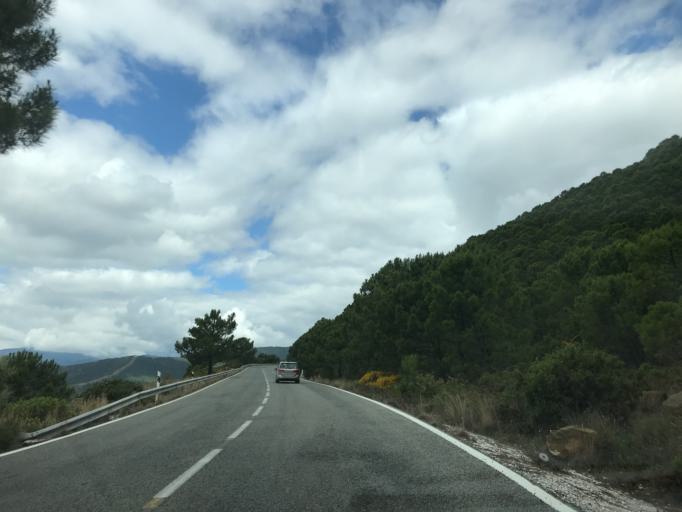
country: ES
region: Andalusia
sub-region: Provincia de Malaga
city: Benahavis
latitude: 36.5586
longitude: -5.0471
